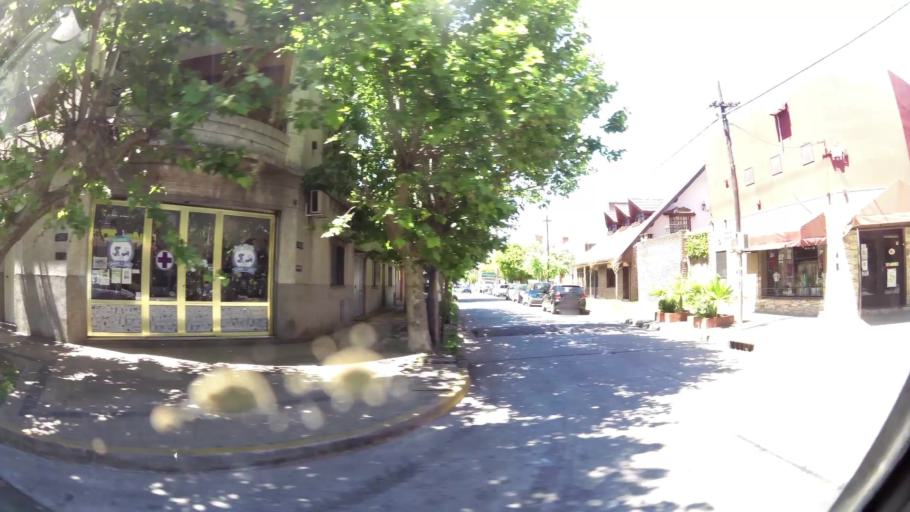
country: AR
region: Buenos Aires
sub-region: Partido de Quilmes
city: Quilmes
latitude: -34.7166
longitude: -58.2995
